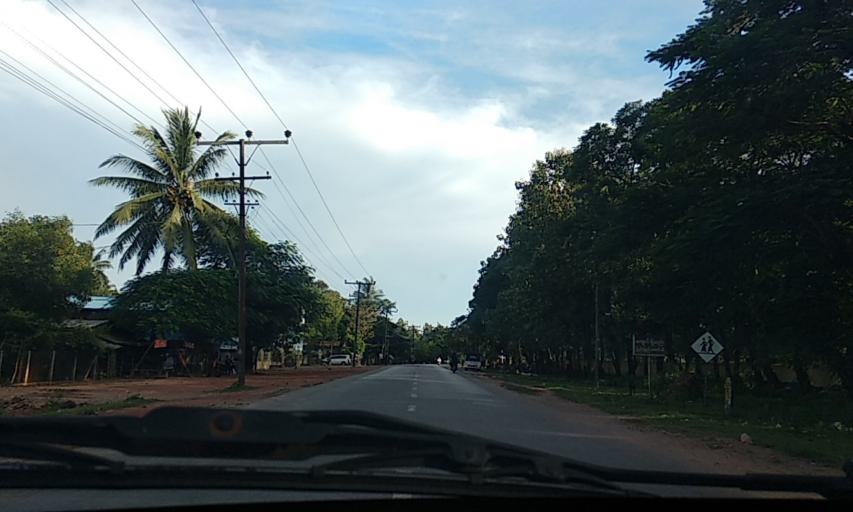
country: MM
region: Mon
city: Mawlamyine
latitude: 16.4068
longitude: 97.7015
